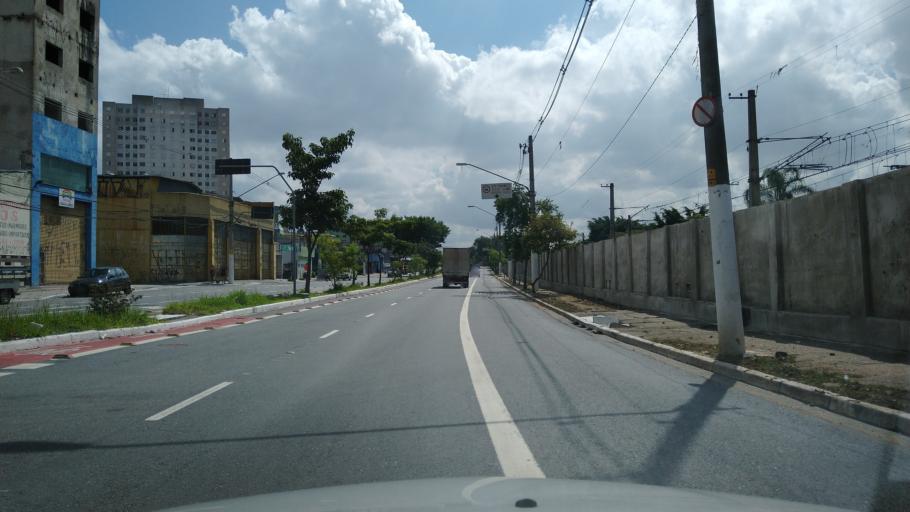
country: BR
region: Sao Paulo
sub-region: Guarulhos
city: Guarulhos
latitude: -23.4847
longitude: -46.4886
